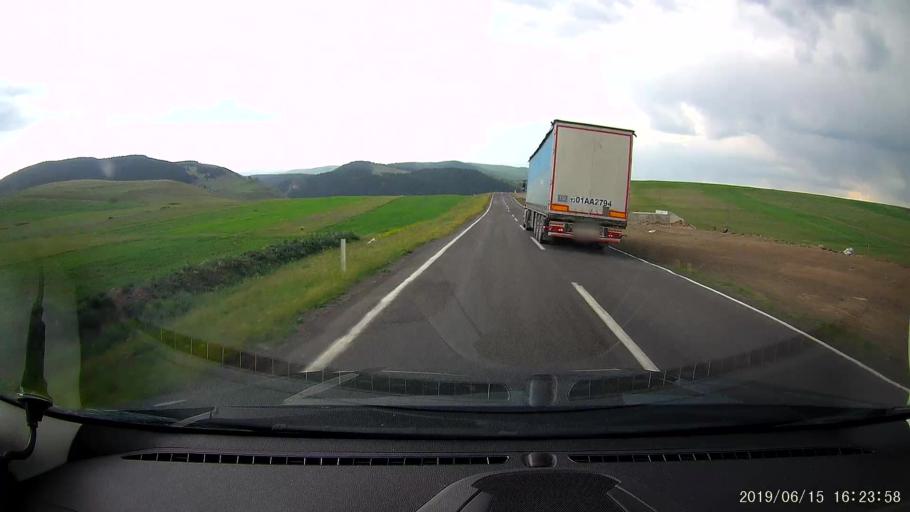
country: TR
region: Ardahan
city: Hanak
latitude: 41.1713
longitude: 42.8675
